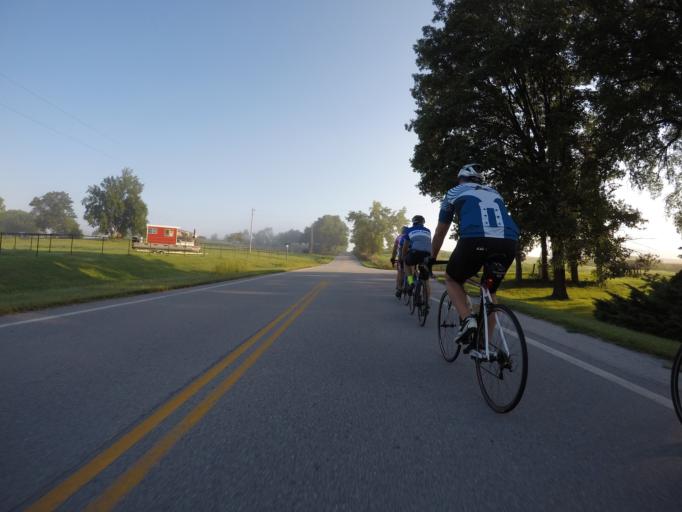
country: US
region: Kansas
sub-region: Leavenworth County
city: Lansing
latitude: 39.2256
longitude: -94.8631
